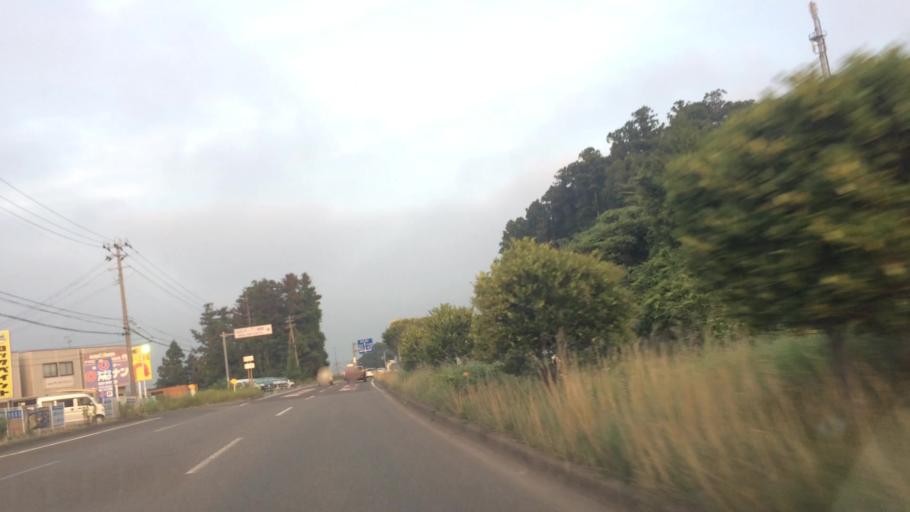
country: JP
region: Miyagi
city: Sendai-shi
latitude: 38.3038
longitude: 140.9175
